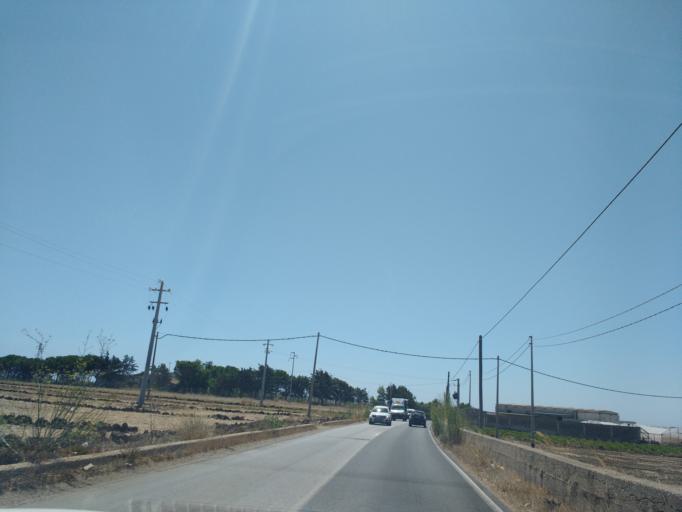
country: IT
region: Sicily
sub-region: Provincia di Siracusa
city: Pachino
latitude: 36.7077
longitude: 15.0768
